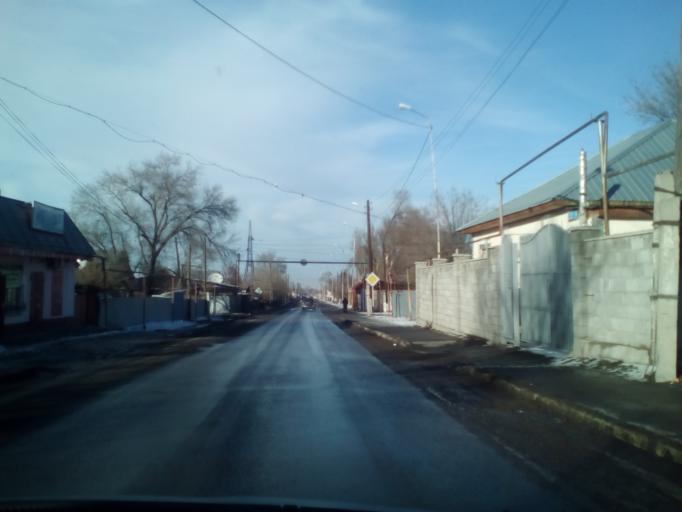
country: KZ
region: Almaty Oblysy
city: Burunday
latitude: 43.1673
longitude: 76.4166
